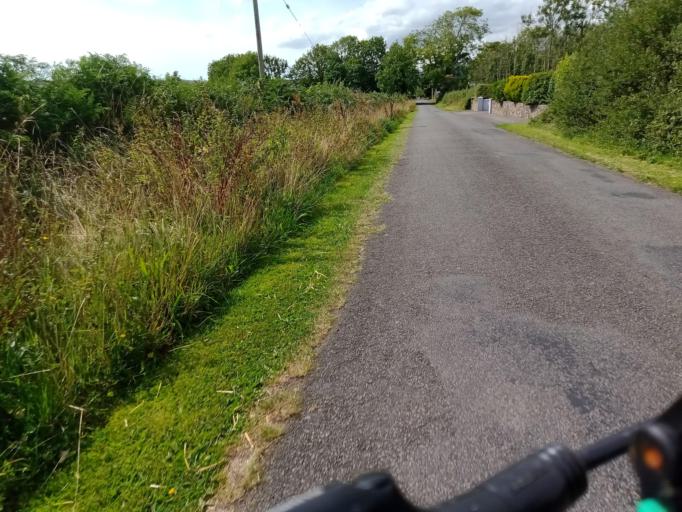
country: IE
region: Munster
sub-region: Waterford
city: Dungarvan
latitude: 52.1402
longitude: -7.4949
